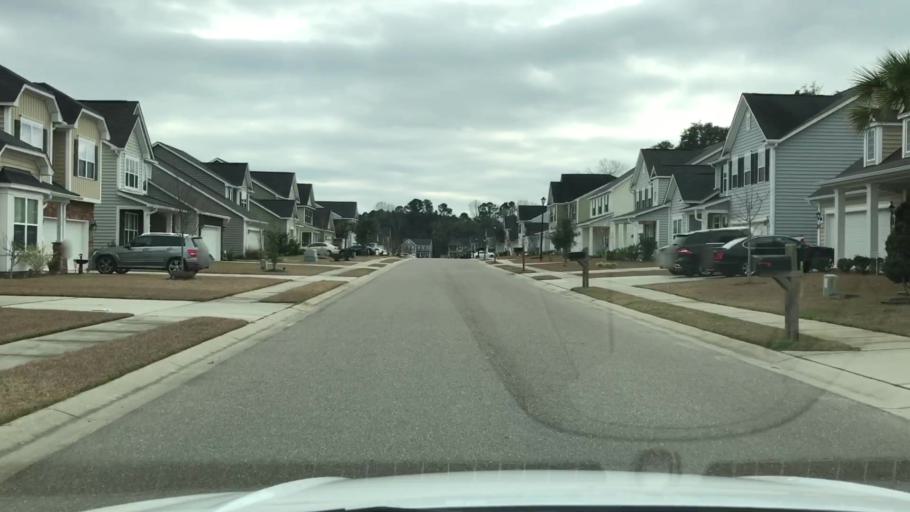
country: US
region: South Carolina
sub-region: Berkeley County
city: Goose Creek
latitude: 33.0301
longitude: -80.0227
